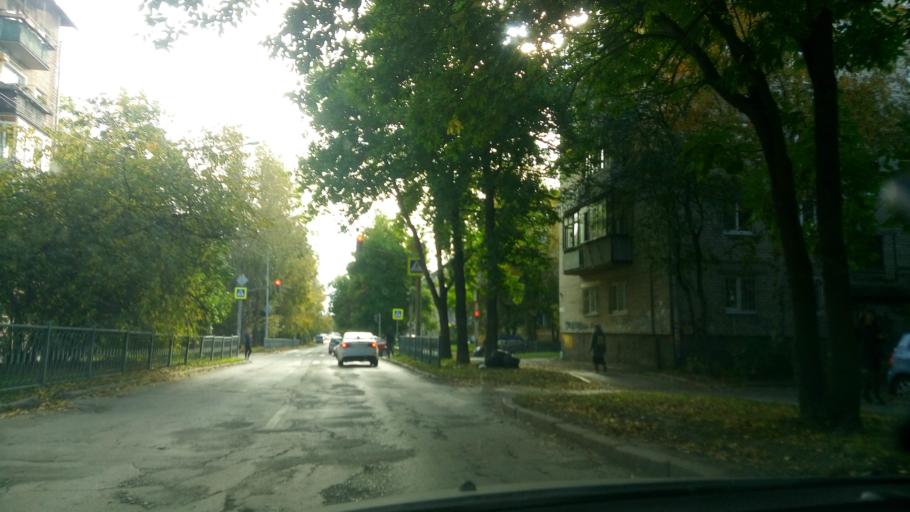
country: RU
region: Sverdlovsk
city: Yekaterinburg
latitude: 56.9014
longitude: 60.6011
